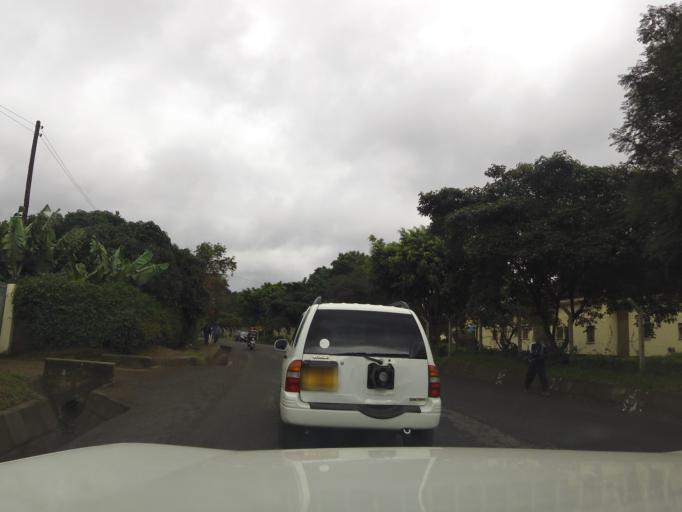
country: TZ
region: Arusha
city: Arusha
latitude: -3.3628
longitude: 36.6901
